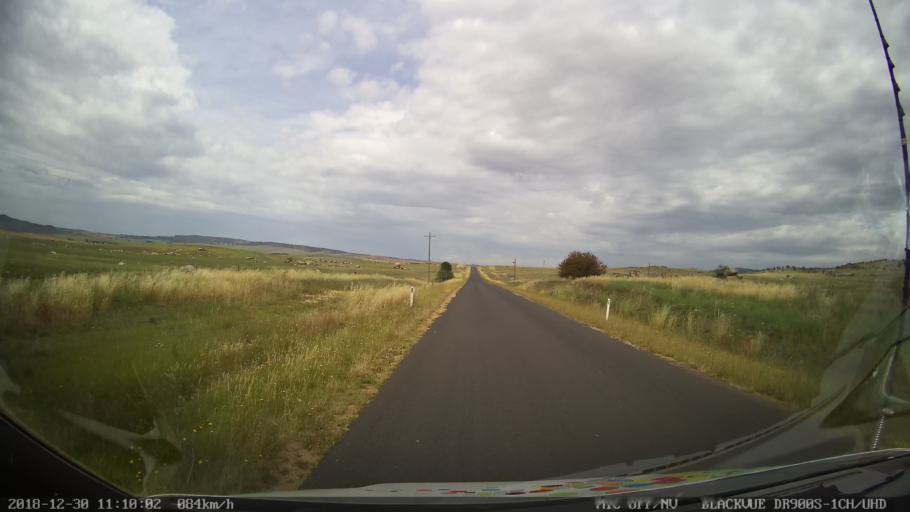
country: AU
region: New South Wales
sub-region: Snowy River
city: Berridale
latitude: -36.5110
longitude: 148.7861
